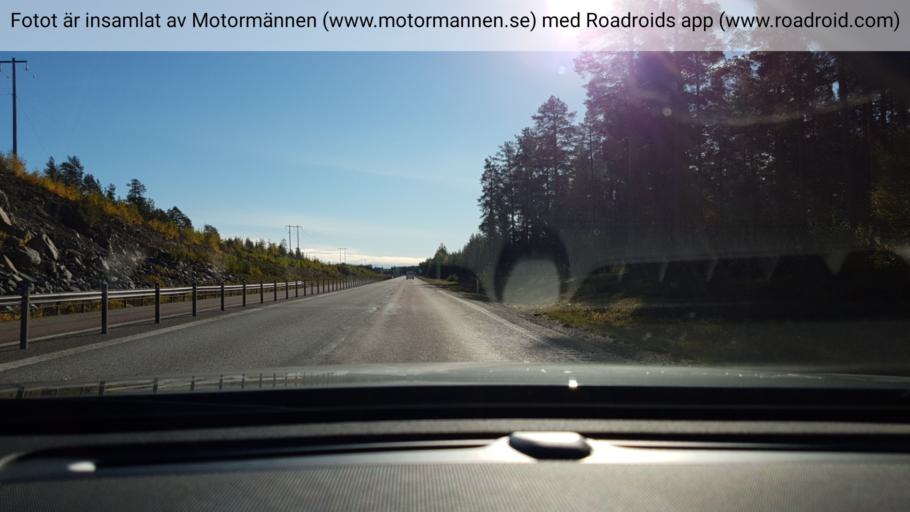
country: SE
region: Vaesterbotten
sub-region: Skelleftea Kommun
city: Soedra Bergsbyn
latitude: 64.6562
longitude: 21.1196
